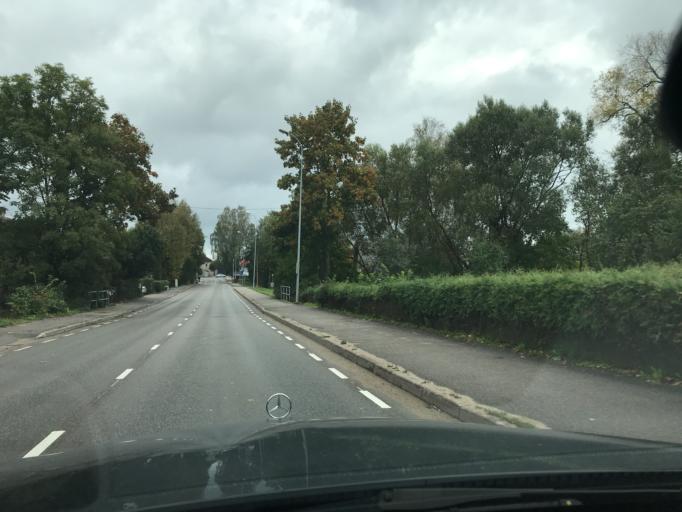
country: EE
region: Valgamaa
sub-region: Torva linn
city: Torva
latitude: 58.0048
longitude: 25.9198
